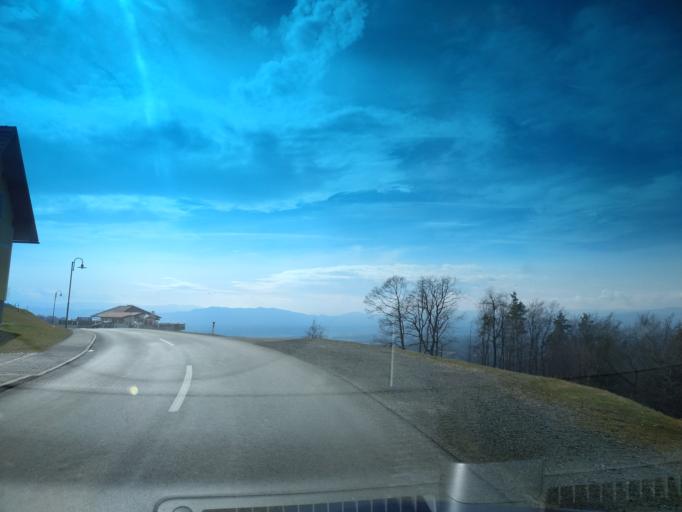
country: AT
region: Styria
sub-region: Politischer Bezirk Leibnitz
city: Kitzeck im Sausal
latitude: 46.7990
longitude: 15.4239
